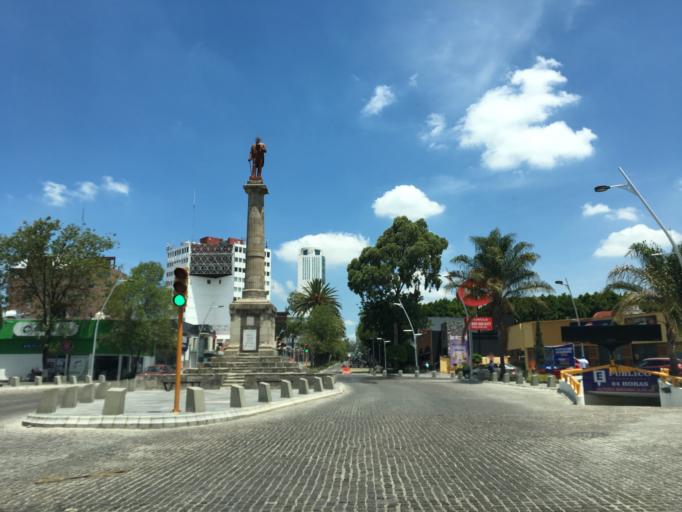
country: MX
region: Puebla
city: Puebla
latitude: 19.0513
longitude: -98.2176
